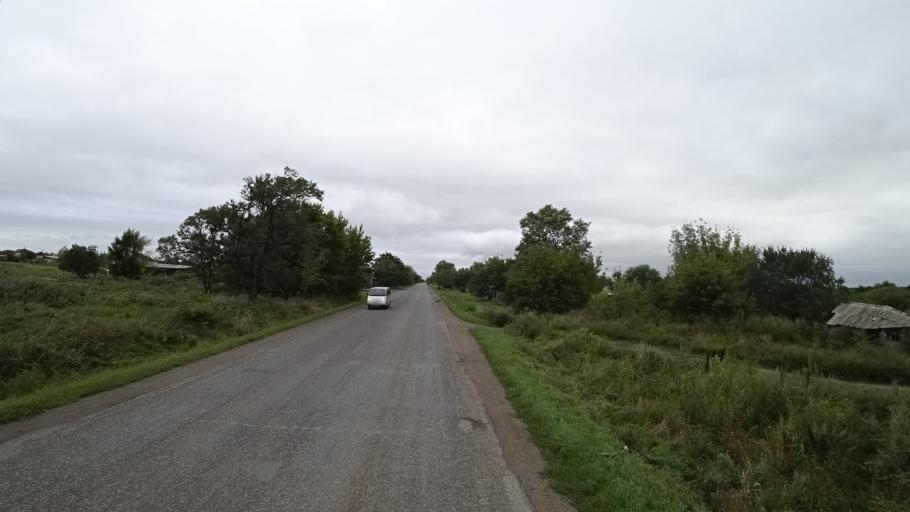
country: RU
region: Primorskiy
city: Chernigovka
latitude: 44.3271
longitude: 132.6029
